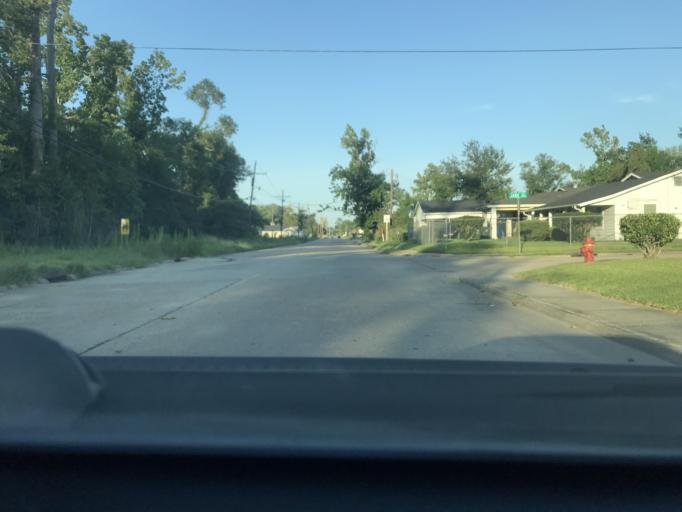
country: US
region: Louisiana
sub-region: Calcasieu Parish
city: Moss Bluff
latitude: 30.2641
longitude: -93.1861
